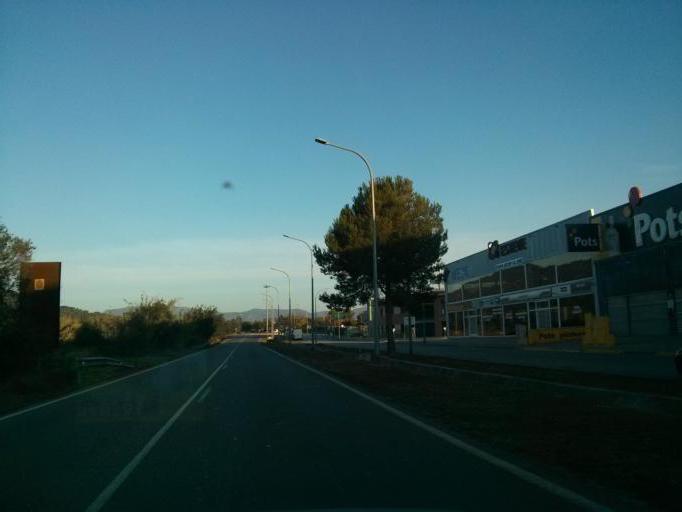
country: ES
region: Catalonia
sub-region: Provincia de Tarragona
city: El Vendrell
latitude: 41.2305
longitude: 1.5293
